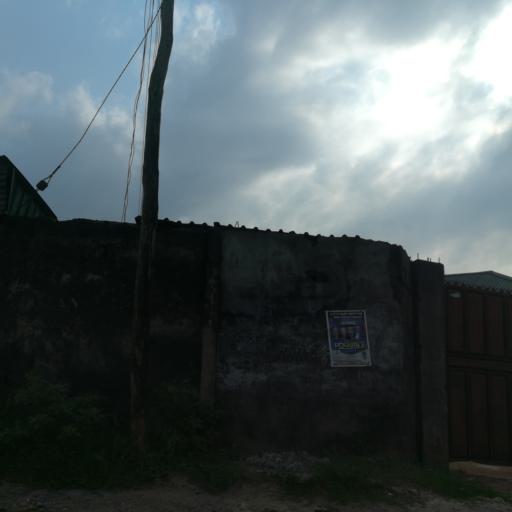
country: NG
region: Rivers
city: Okrika
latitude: 4.7783
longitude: 7.1321
